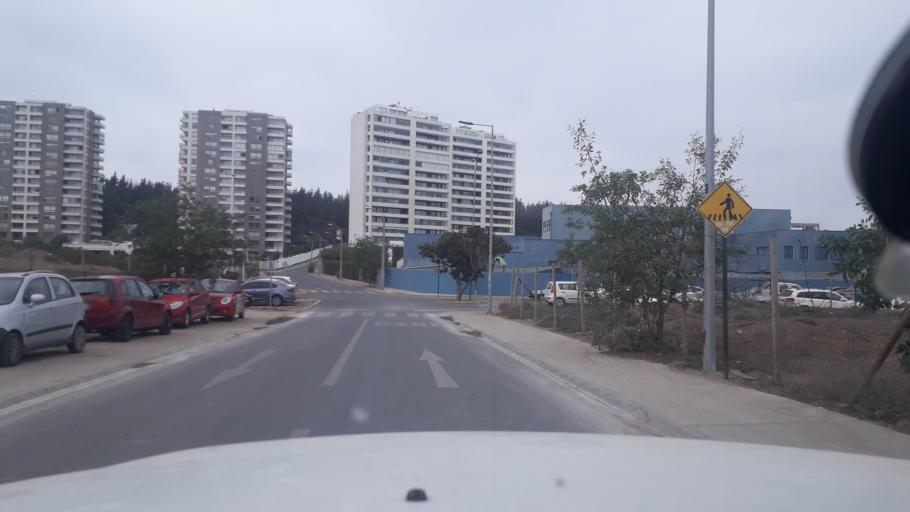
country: CL
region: Valparaiso
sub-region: Provincia de Valparaiso
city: Vina del Mar
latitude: -32.9571
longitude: -71.5418
